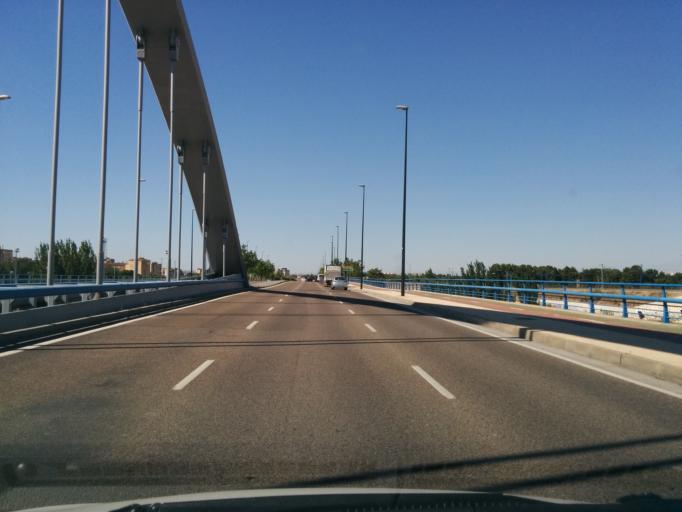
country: ES
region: Aragon
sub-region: Provincia de Zaragoza
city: Zaragoza
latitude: 41.6510
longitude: -0.8546
